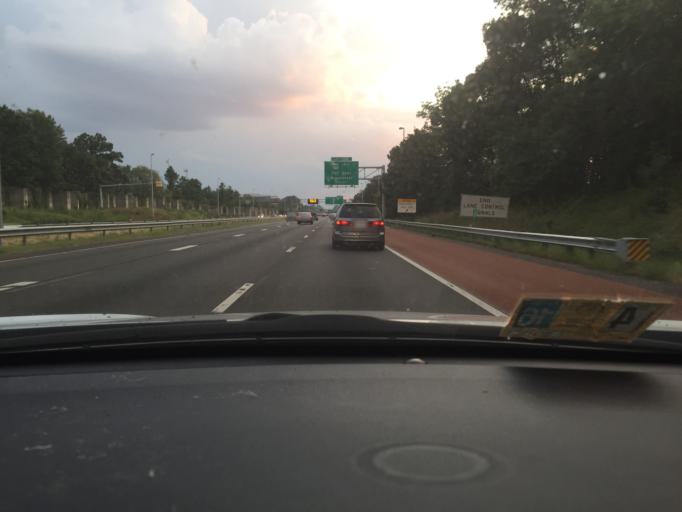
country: US
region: Virginia
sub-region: City of Fairfax
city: Fairfax
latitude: 38.8662
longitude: -77.3250
